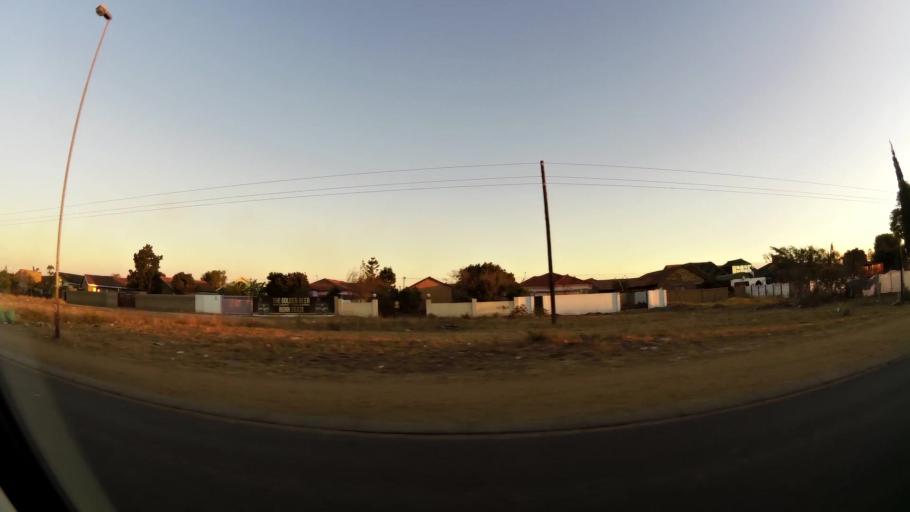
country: ZA
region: Limpopo
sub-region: Capricorn District Municipality
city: Polokwane
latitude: -23.8534
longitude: 29.3750
